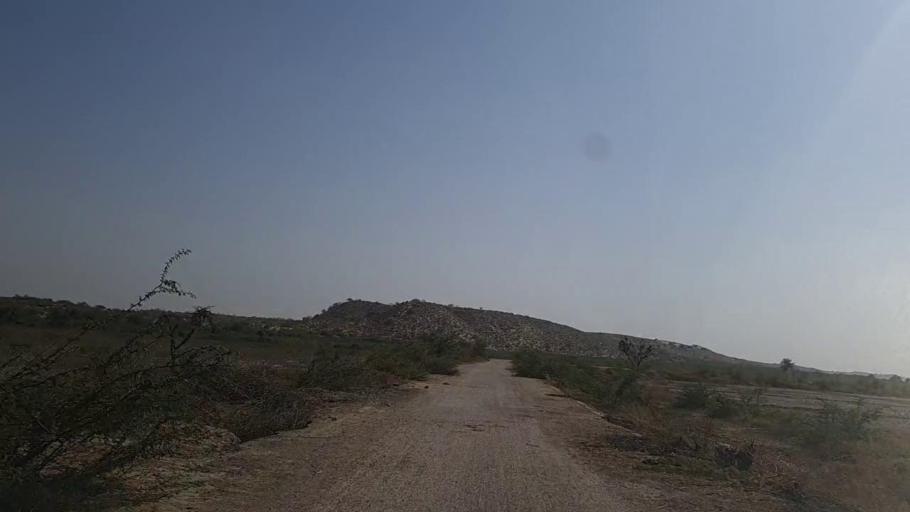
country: PK
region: Sindh
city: Naukot
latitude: 24.5941
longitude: 69.3084
